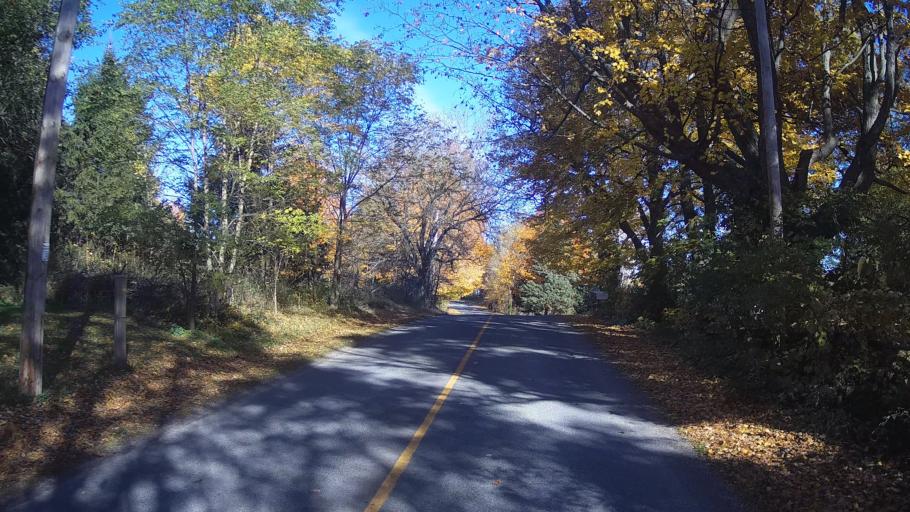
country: CA
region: Ontario
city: Kingston
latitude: 44.4488
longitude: -76.5129
